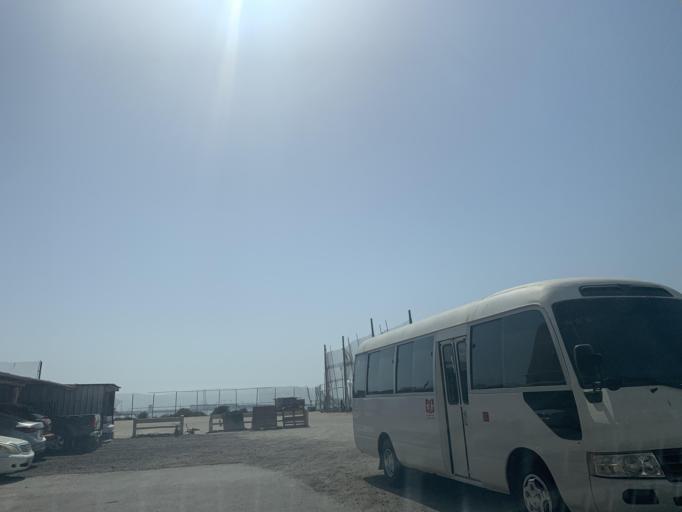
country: BH
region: Manama
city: Jidd Hafs
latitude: 26.2361
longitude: 50.4993
